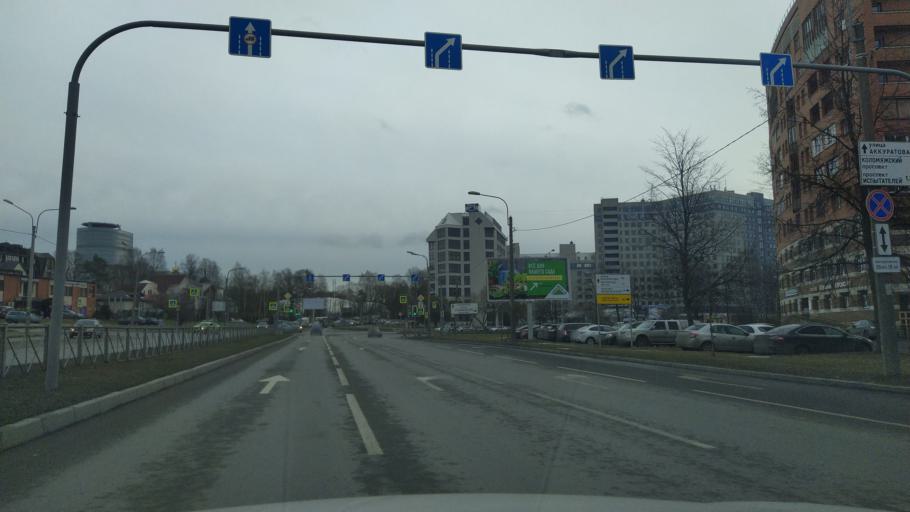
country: RU
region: St.-Petersburg
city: Kolomyagi
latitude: 60.0155
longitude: 30.2917
